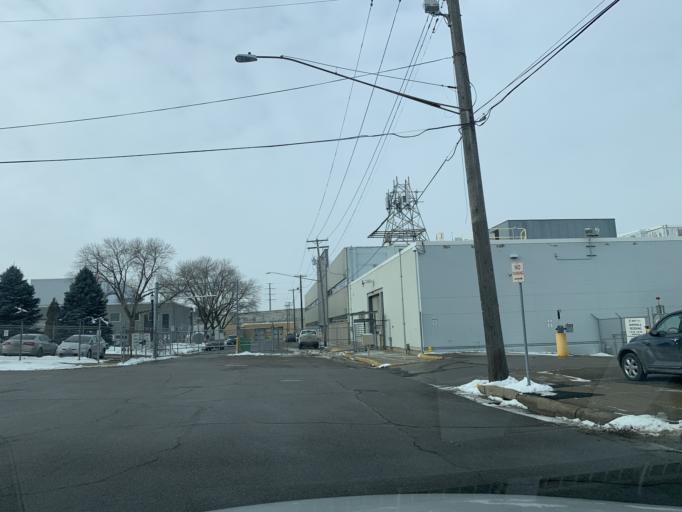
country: US
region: Minnesota
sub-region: Hennepin County
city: Minneapolis
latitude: 44.9770
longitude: -93.2839
